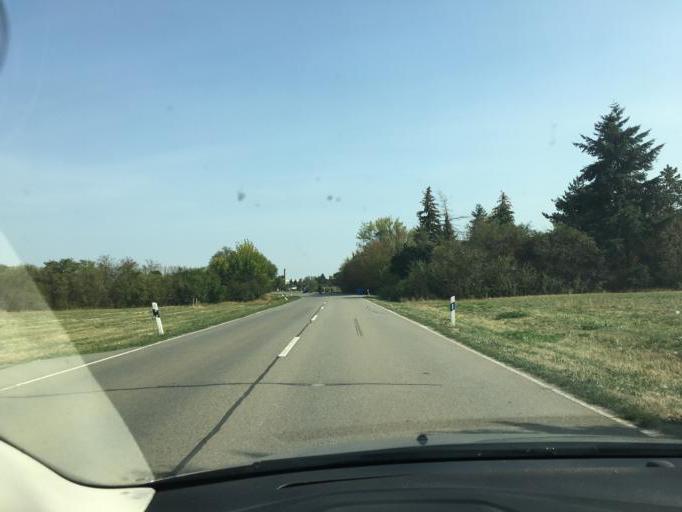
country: DE
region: Saxony-Anhalt
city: Barby
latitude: 51.9797
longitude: 11.8666
